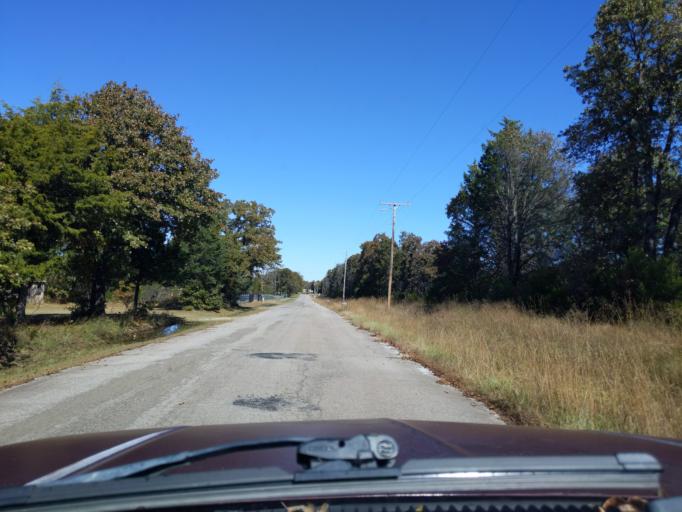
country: US
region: Oklahoma
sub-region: Creek County
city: Bristow
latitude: 35.7006
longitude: -96.4098
